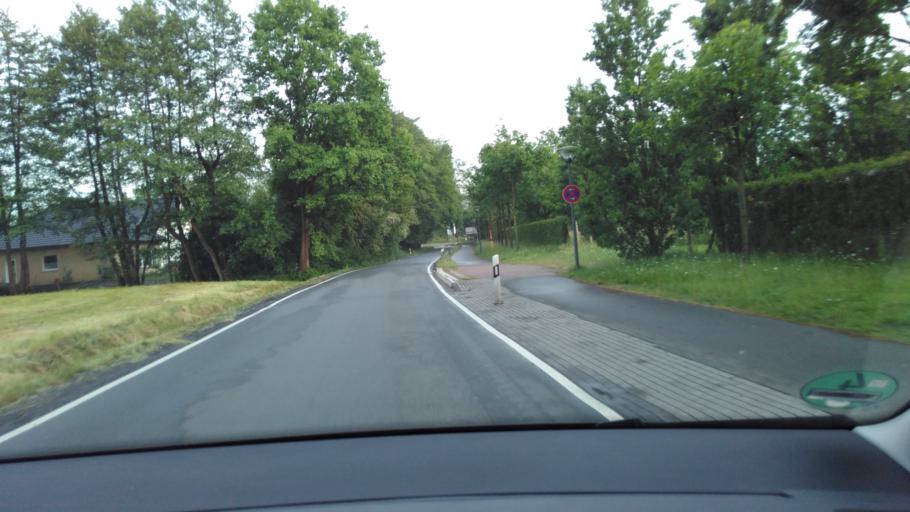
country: DE
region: North Rhine-Westphalia
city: Rietberg
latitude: 51.8213
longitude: 8.4462
